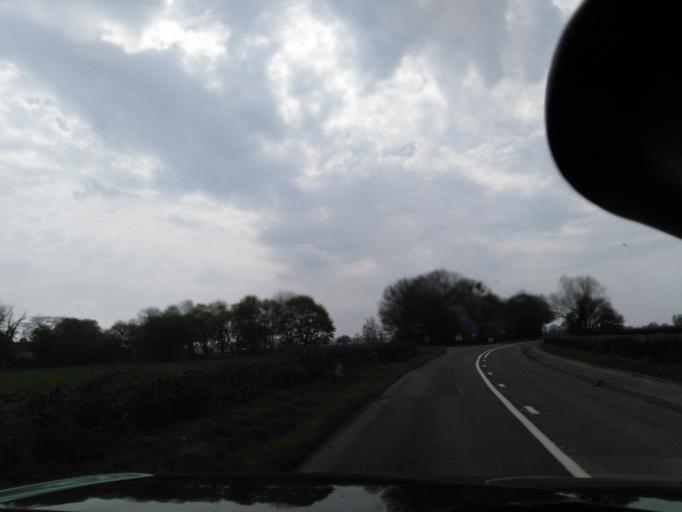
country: GB
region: England
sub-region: Wiltshire
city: Malmesbury
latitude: 51.5692
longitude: -2.0985
